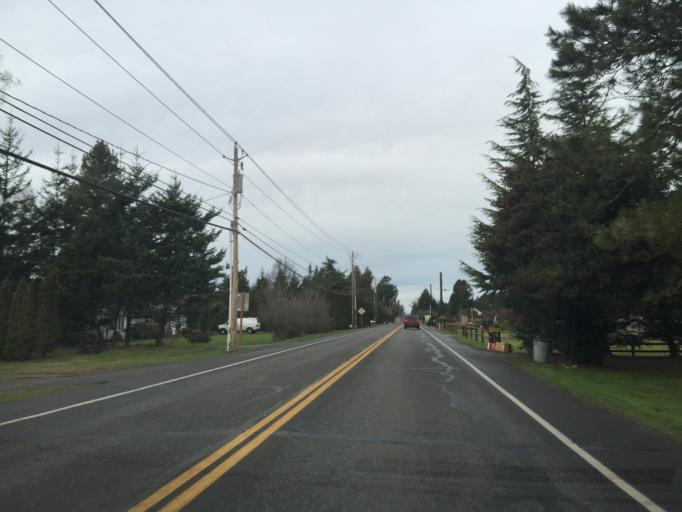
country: US
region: Washington
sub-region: Whatcom County
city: Marietta-Alderwood
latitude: 48.8362
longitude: -122.5409
